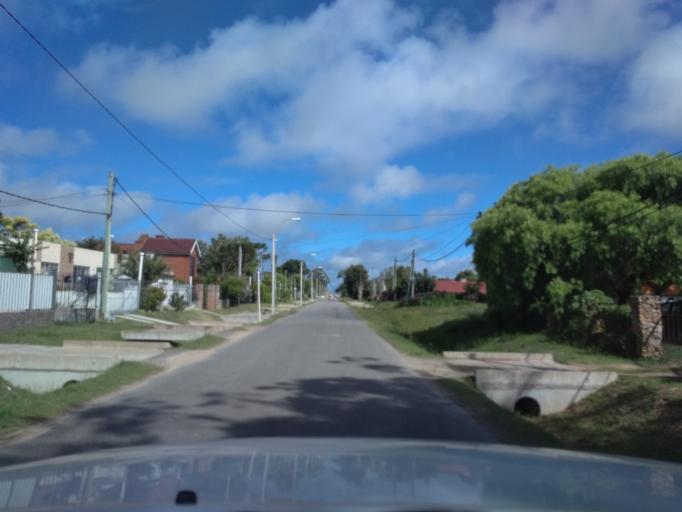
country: UY
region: Canelones
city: Barra de Carrasco
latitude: -34.8339
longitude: -55.9729
